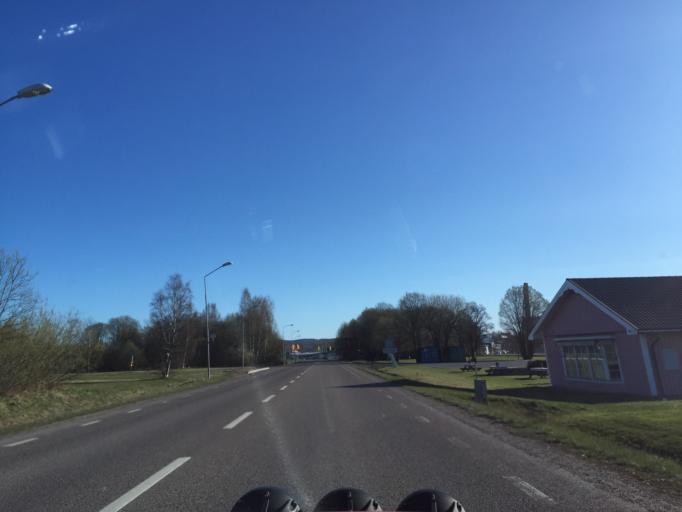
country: SE
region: Dalarna
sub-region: Borlange Kommun
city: Borlaenge
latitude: 60.4726
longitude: 15.4014
